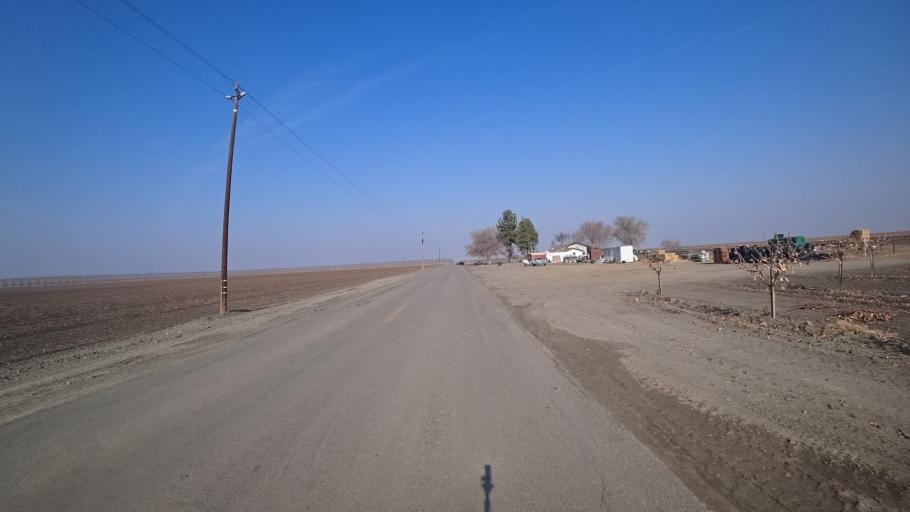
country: US
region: California
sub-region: Kern County
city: Buttonwillow
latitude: 35.3567
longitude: -119.4123
